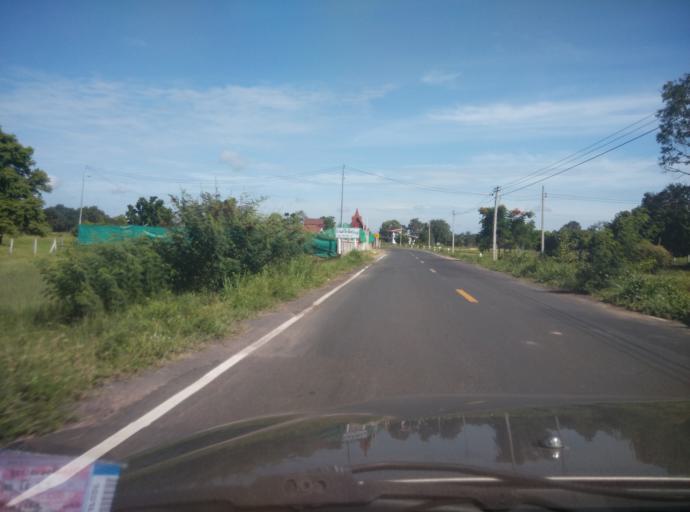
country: TH
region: Sisaket
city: Si Sa Ket
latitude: 15.1183
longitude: 104.2533
